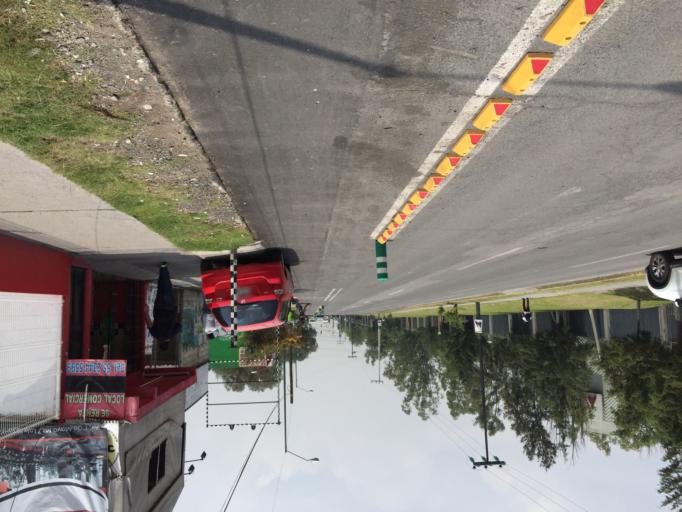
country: MX
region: Mexico
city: Cuautitlan Izcalli
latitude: 19.6362
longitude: -99.2065
